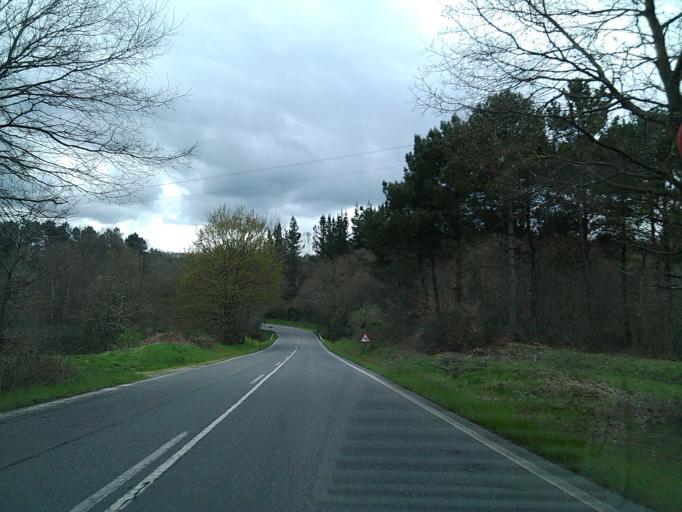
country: ES
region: Galicia
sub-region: Provincia de Lugo
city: Guitiriz
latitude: 43.1758
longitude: -7.8316
